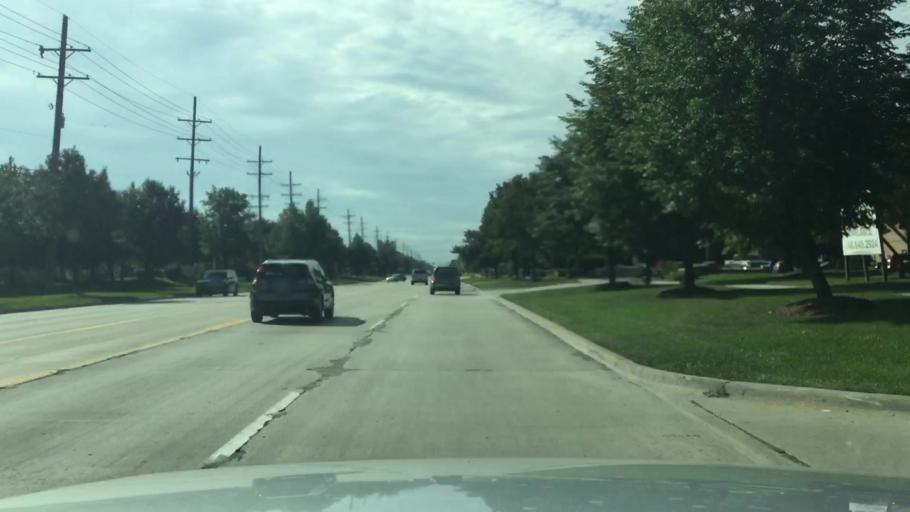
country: US
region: Michigan
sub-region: Wayne County
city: Canton
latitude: 42.3195
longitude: -83.4879
